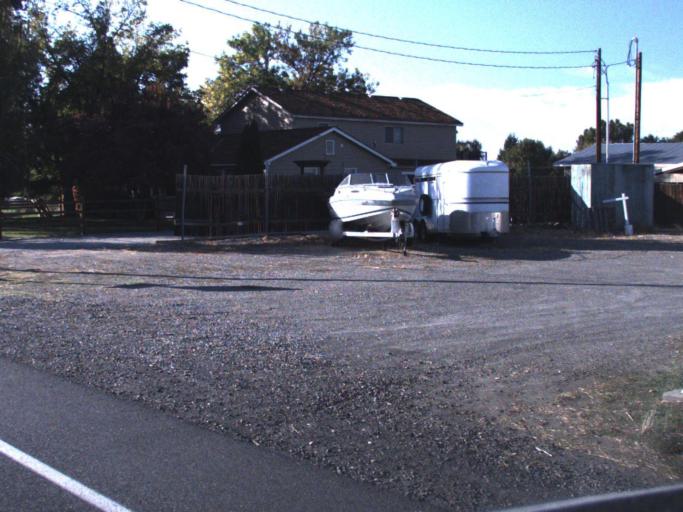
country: US
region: Washington
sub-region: Walla Walla County
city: Burbank
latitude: 46.2117
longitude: -119.0048
